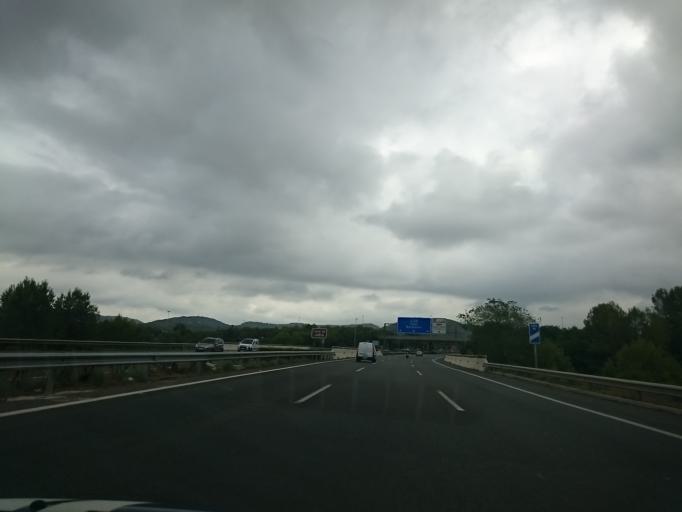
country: ES
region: Catalonia
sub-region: Provincia de Barcelona
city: Sant Pere de Ribes
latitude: 41.2494
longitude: 1.7827
